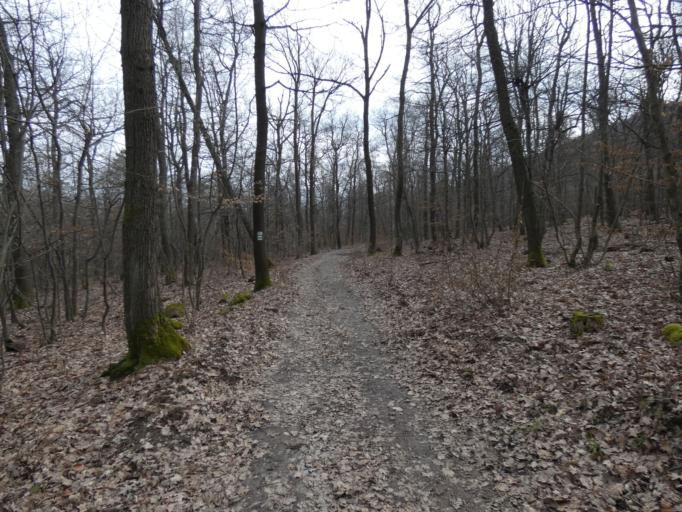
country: HU
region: Pest
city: Pilisborosjeno
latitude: 47.6284
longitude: 18.9817
